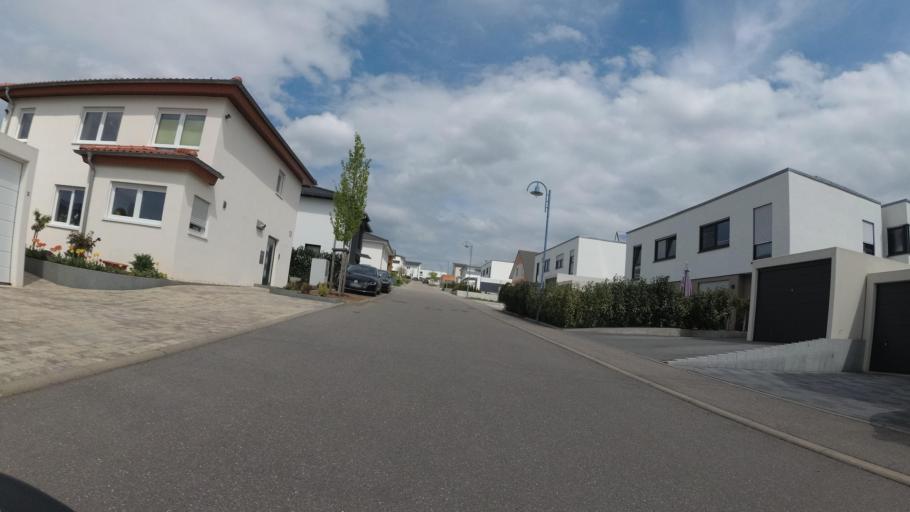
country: DE
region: Baden-Wuerttemberg
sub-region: Regierungsbezirk Stuttgart
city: Neuenstadt am Kocher
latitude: 49.2435
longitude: 9.3308
